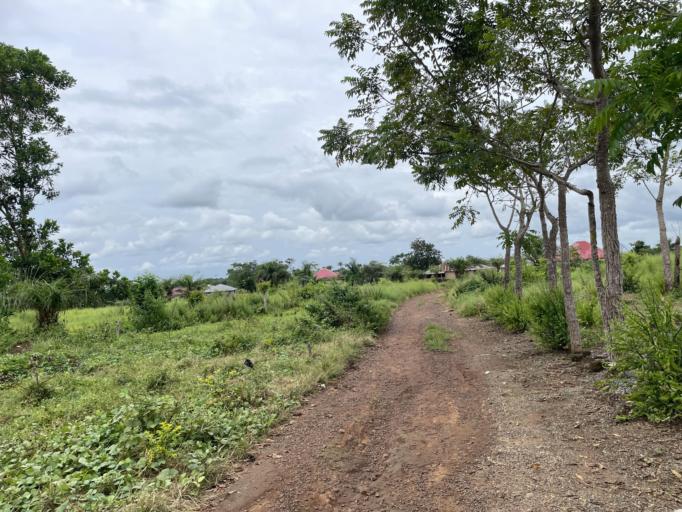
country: SL
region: Northern Province
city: Kambia
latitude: 9.1312
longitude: -12.9079
